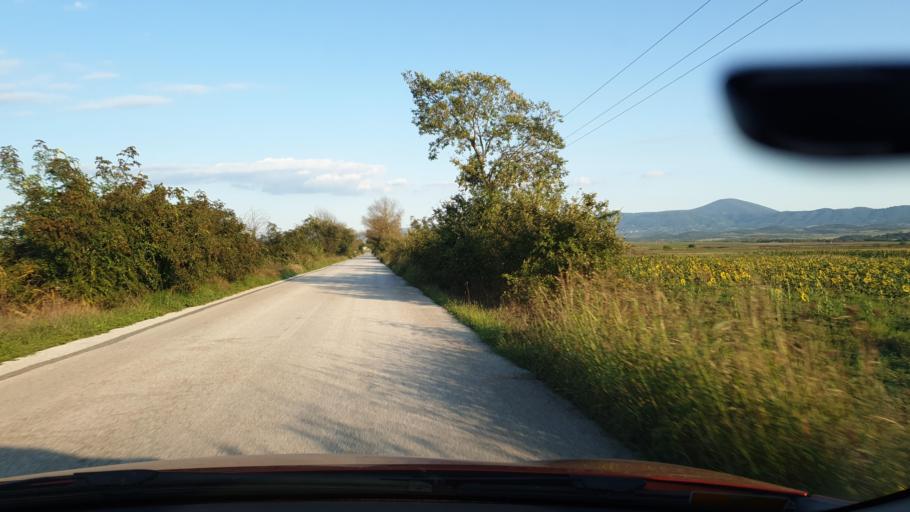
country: GR
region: Central Macedonia
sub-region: Nomos Thessalonikis
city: Nea Apollonia
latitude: 40.5598
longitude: 23.3513
